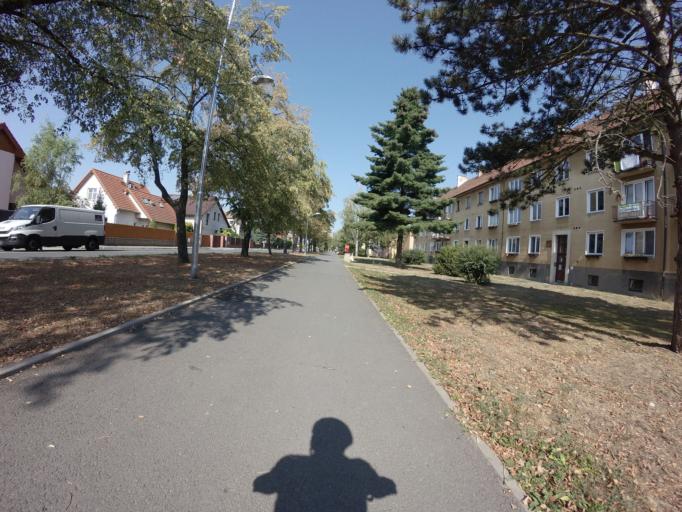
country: CZ
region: Central Bohemia
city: Tynec nad Sazavou
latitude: 49.8357
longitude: 14.5862
